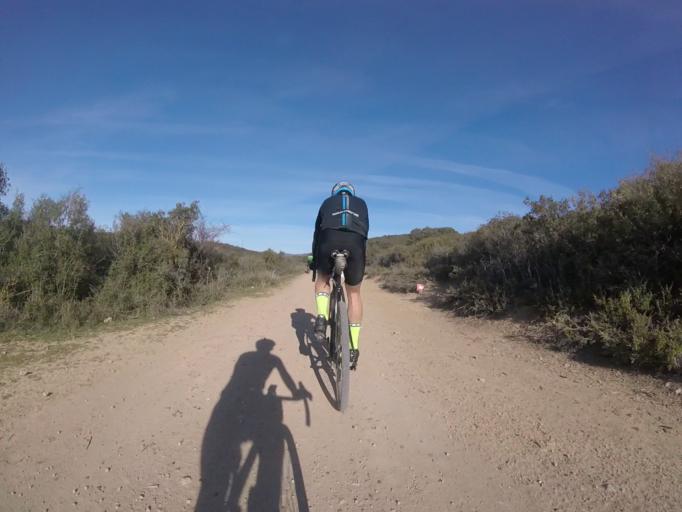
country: ES
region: Navarre
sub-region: Provincia de Navarra
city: Yerri
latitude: 42.6974
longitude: -1.9627
